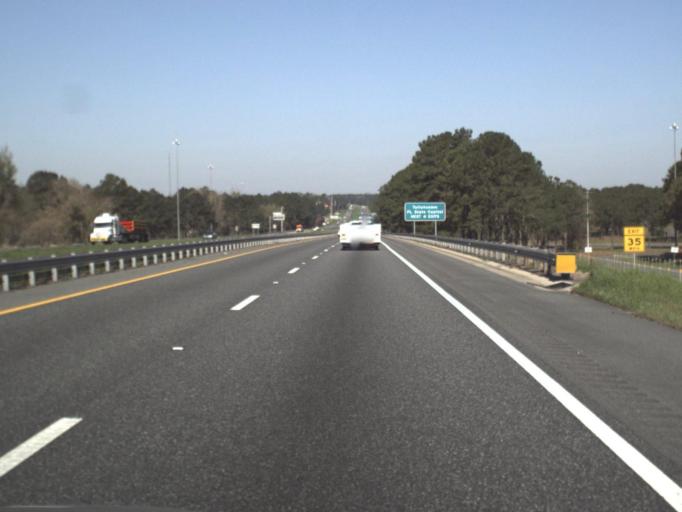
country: US
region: Florida
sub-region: Leon County
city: Tallahassee
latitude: 30.4827
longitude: -84.1544
